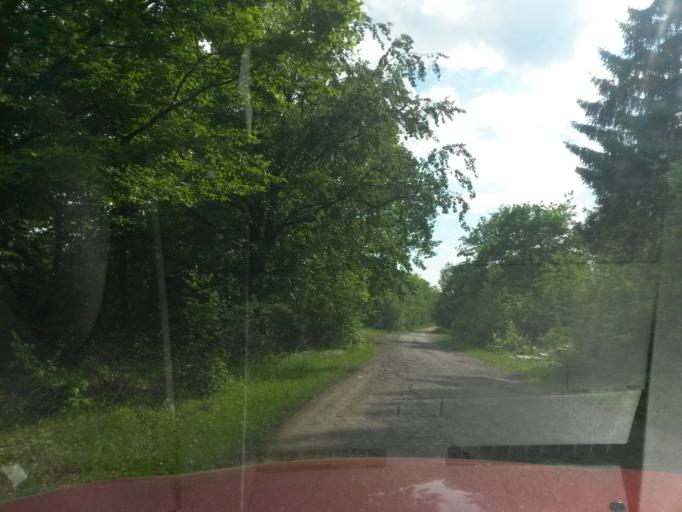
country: UA
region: Zakarpattia
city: Velykyi Bereznyi
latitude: 48.9005
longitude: 22.5173
